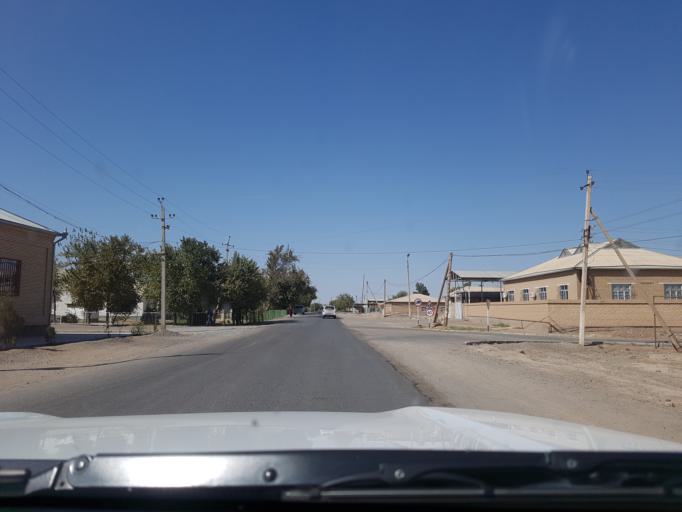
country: IR
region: Razavi Khorasan
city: Sarakhs
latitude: 36.5191
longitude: 61.2194
